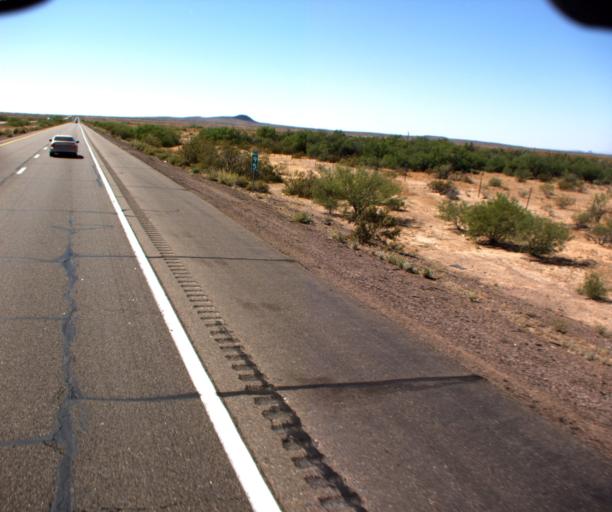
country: US
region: Arizona
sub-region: Maricopa County
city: Gila Bend
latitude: 32.8869
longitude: -113.0808
